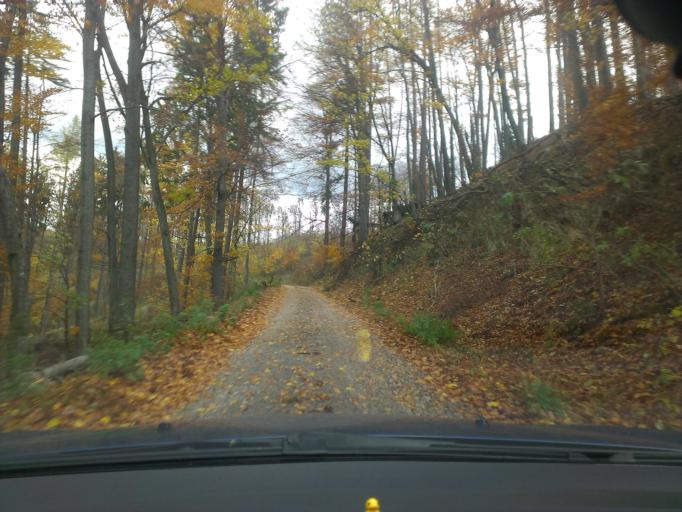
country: SK
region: Trnavsky
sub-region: Okres Trnava
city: Piestany
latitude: 48.6141
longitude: 17.9565
